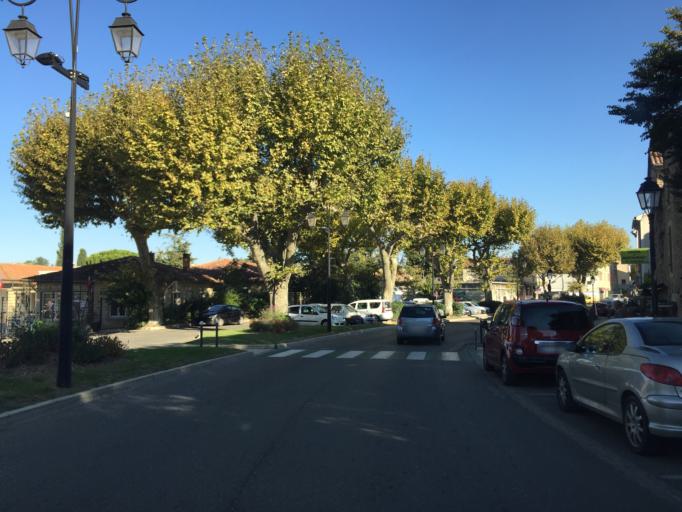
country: FR
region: Provence-Alpes-Cote d'Azur
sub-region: Departement du Vaucluse
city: Bollene
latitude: 44.2795
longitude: 4.7459
